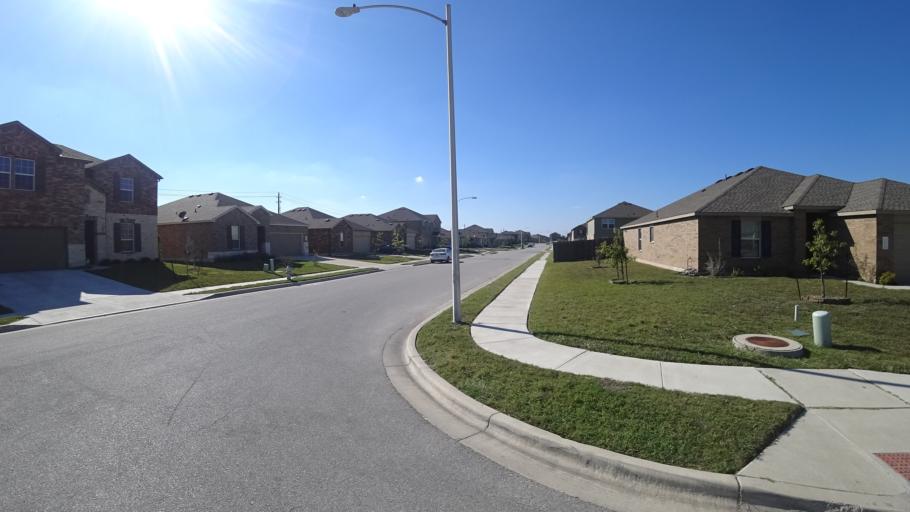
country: US
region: Texas
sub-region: Travis County
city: Manor
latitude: 30.3542
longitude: -97.6191
